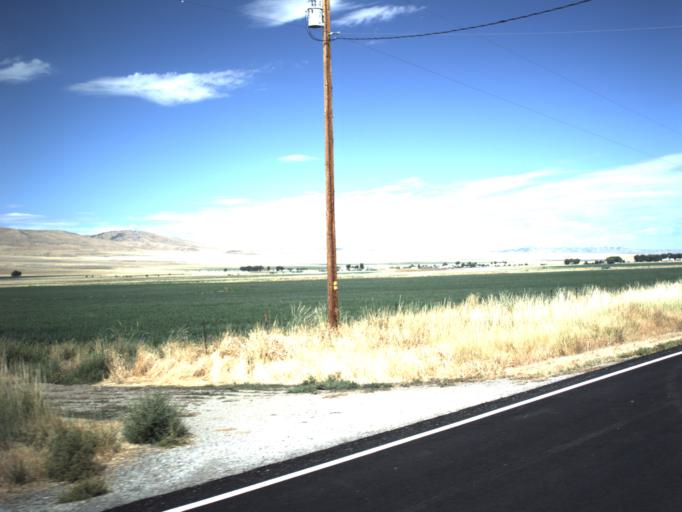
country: US
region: Utah
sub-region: Box Elder County
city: Garland
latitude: 41.7772
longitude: -112.4352
